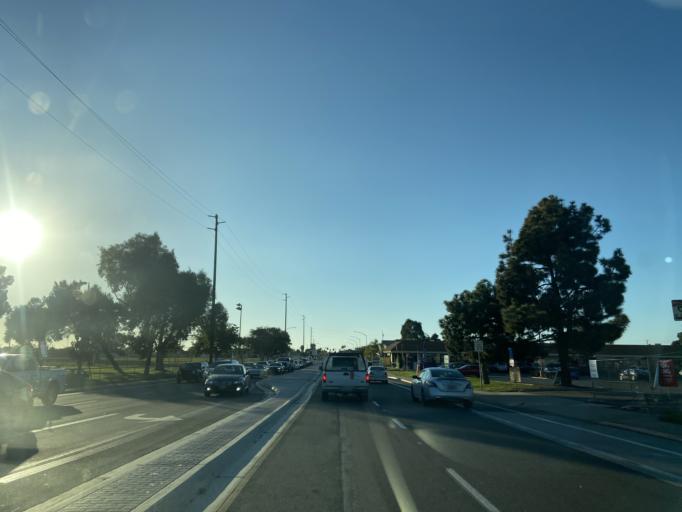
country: US
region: California
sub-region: San Diego County
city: Imperial Beach
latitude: 32.5766
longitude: -117.0931
